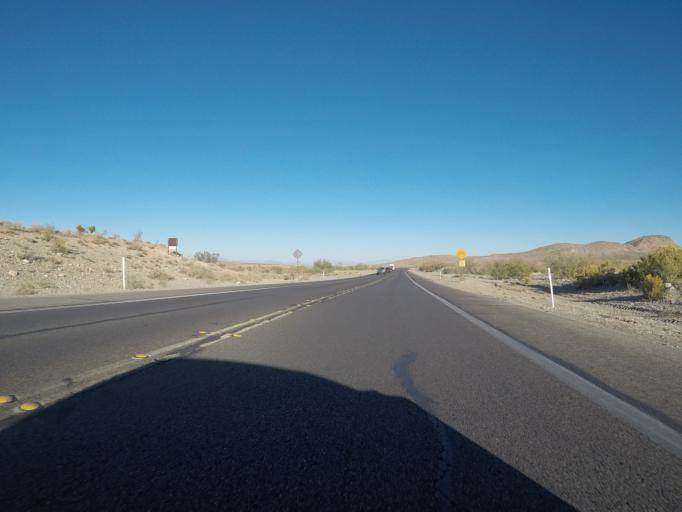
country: US
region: Nevada
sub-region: Clark County
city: Summerlin South
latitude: 36.1431
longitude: -115.3956
